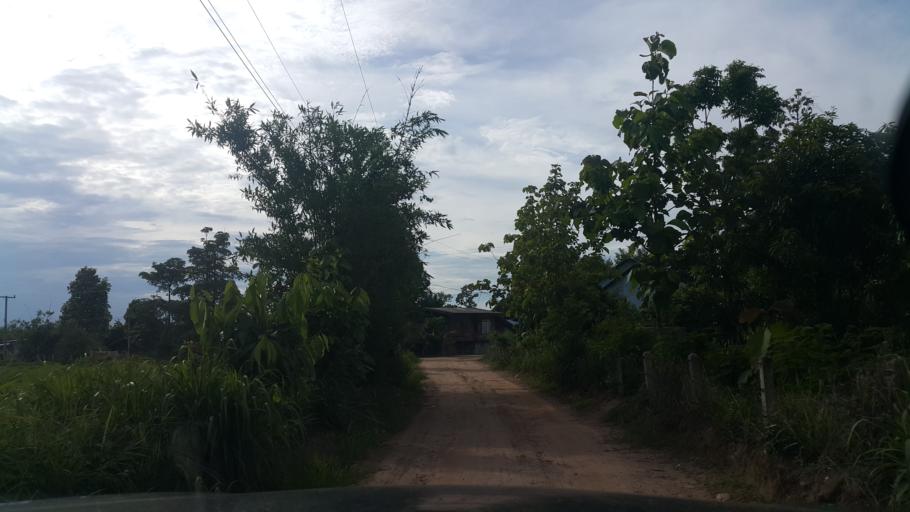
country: TH
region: Chiang Mai
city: Mae On
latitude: 18.7170
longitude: 99.2116
